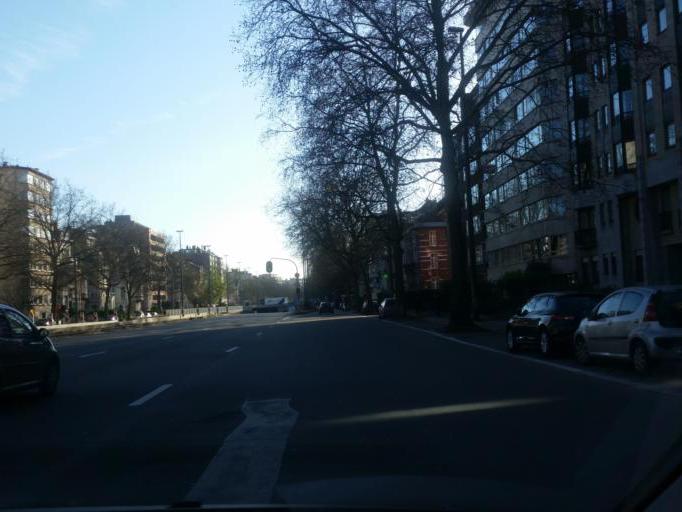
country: BE
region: Brussels Capital
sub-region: Bruxelles-Capitale
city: Brussels
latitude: 50.8447
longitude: 4.4048
